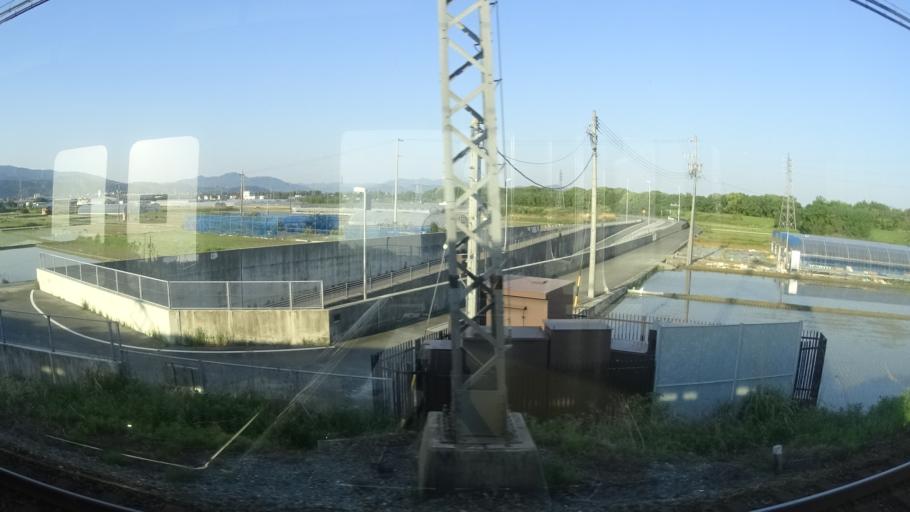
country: JP
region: Mie
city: Ise
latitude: 34.5071
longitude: 136.6925
